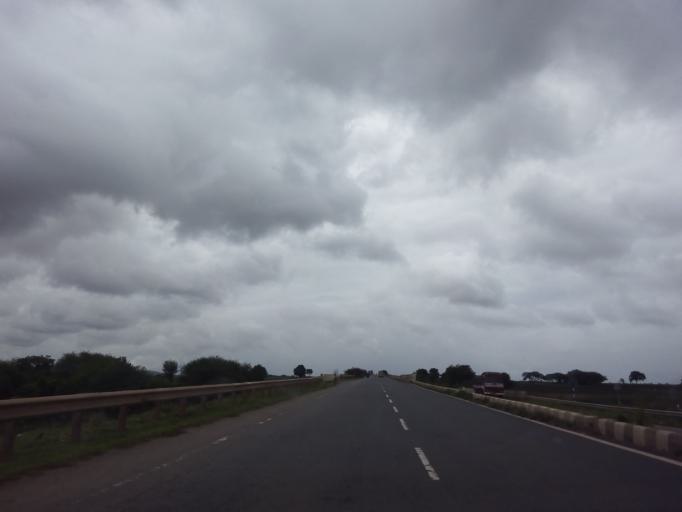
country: IN
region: Karnataka
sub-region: Haveri
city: Haveri
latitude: 14.7560
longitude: 75.4427
